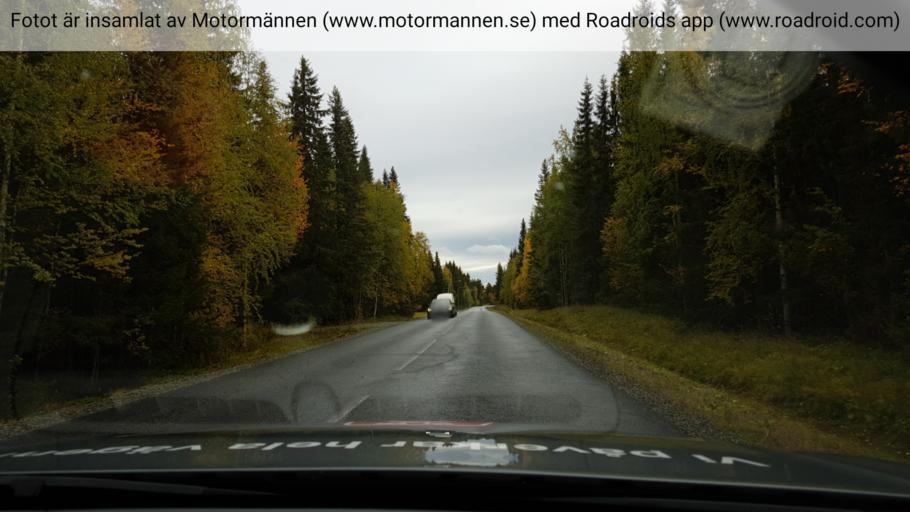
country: SE
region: Vaesterbotten
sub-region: Vilhelmina Kommun
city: Sjoberg
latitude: 64.6714
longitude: 16.2958
